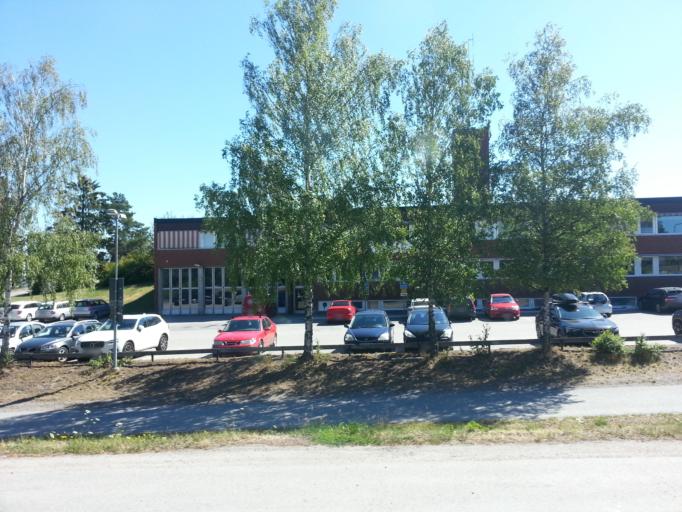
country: SE
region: Stockholm
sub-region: Tyreso Kommun
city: Bollmora
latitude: 59.2435
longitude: 18.2150
